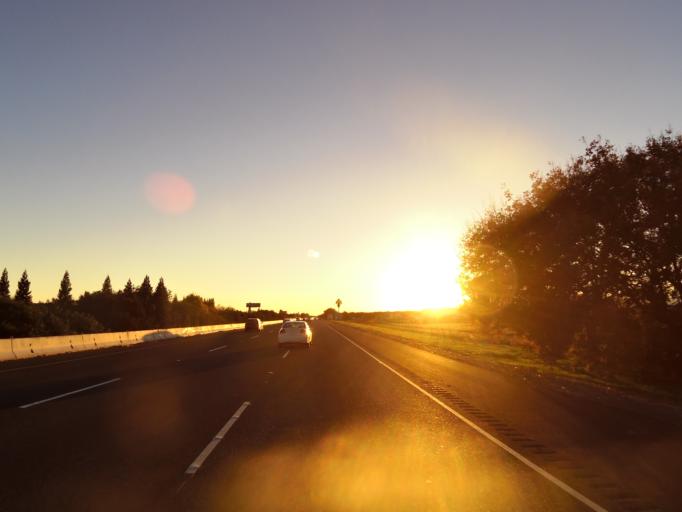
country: US
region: California
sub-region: Solano County
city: Dixon
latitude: 38.4688
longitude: -121.8295
